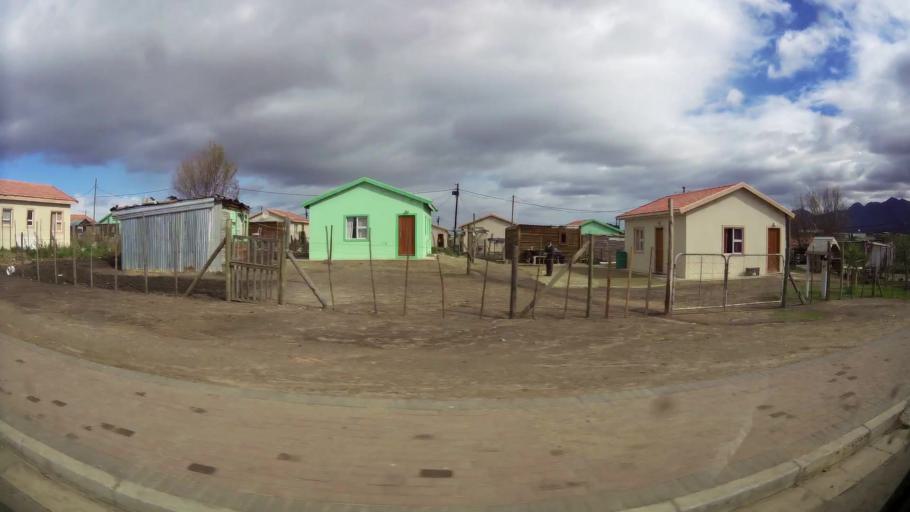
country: ZA
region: Western Cape
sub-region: Eden District Municipality
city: George
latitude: -33.9749
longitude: 22.4893
